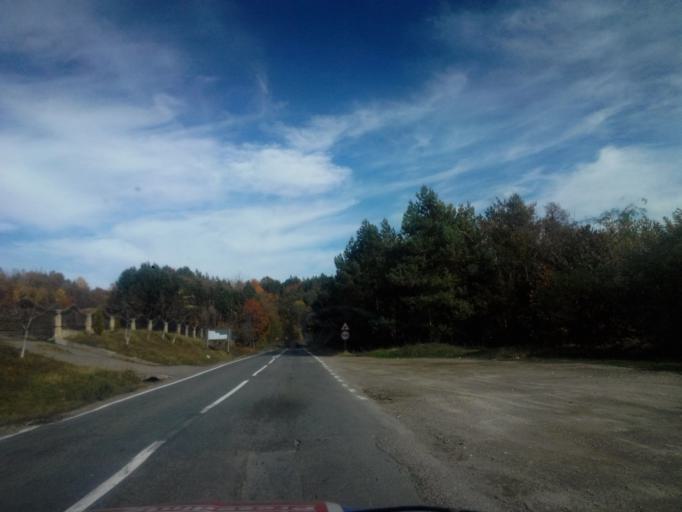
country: RO
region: Bacau
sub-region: Comuna Luizi-Calugara
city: Luizi-Calugara
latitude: 46.4989
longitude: 26.7993
